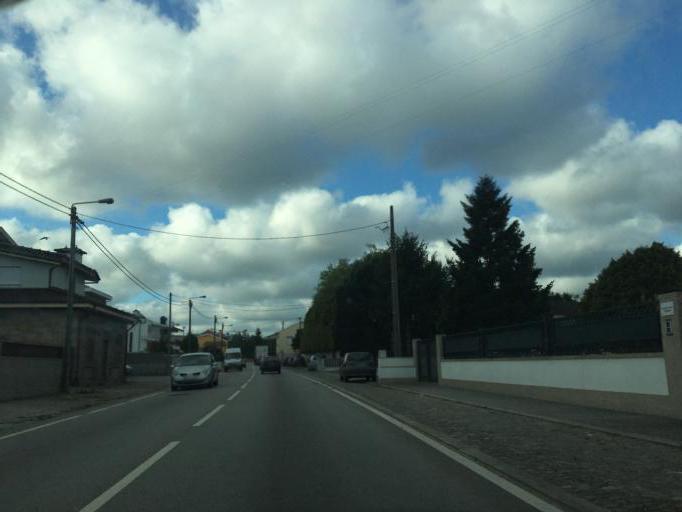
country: PT
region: Porto
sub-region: Maia
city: Anta
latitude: 41.2810
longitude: -8.6059
